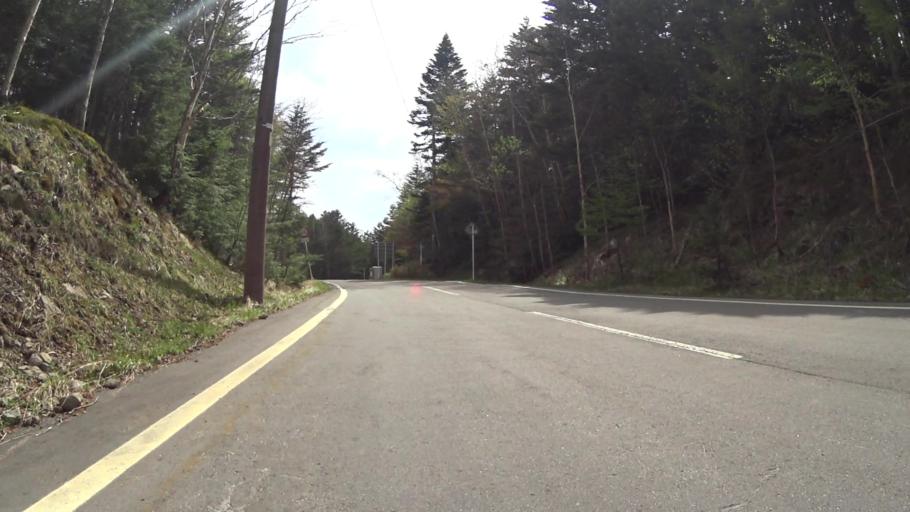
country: JP
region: Nagano
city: Saku
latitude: 36.0630
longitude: 138.3721
